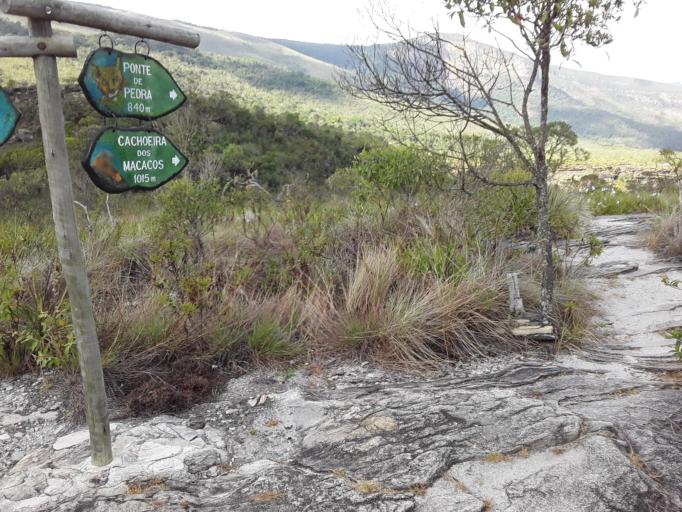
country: BR
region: Minas Gerais
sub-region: Lima Duarte
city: Lima Duarte
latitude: -21.7098
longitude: -43.8948
